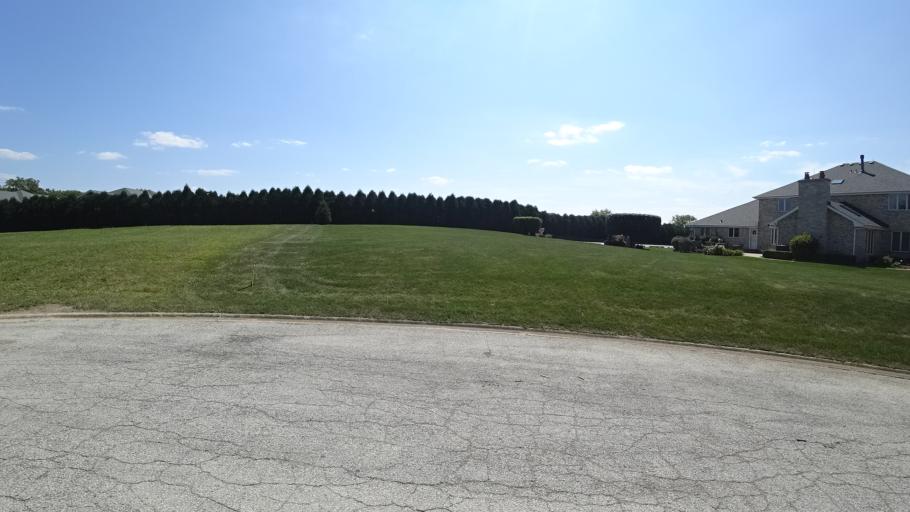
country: US
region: Illinois
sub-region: Cook County
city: Orland Park
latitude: 41.6312
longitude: -87.8811
